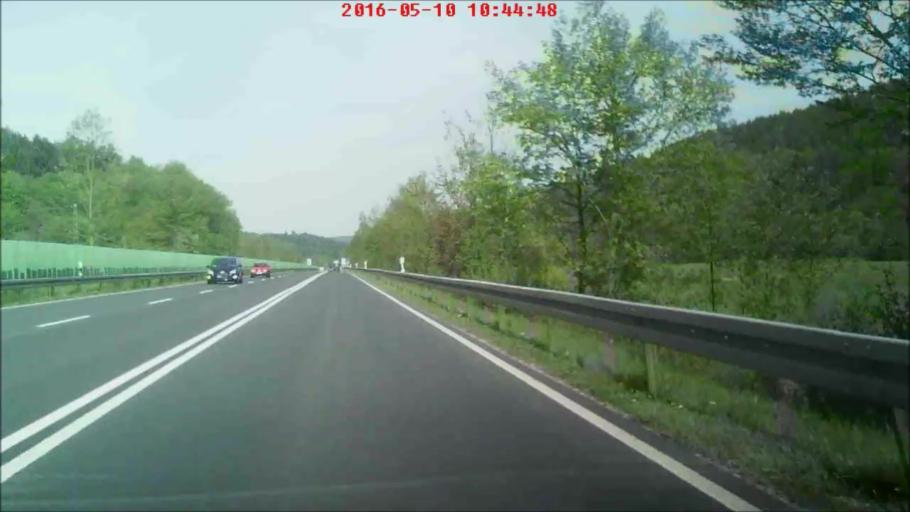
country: DE
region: Hesse
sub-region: Regierungsbezirk Kassel
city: Burghaun
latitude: 50.7238
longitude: 9.7071
